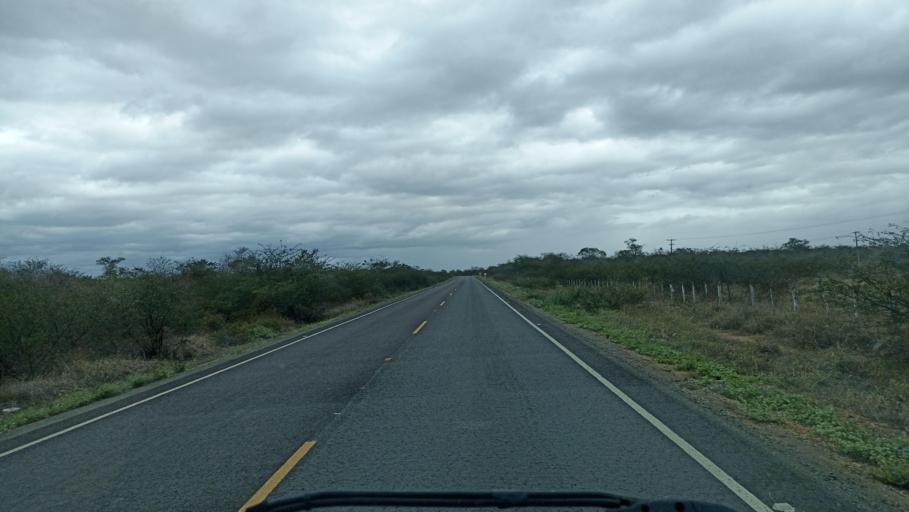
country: BR
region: Bahia
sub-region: Iacu
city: Iacu
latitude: -12.9769
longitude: -40.5139
